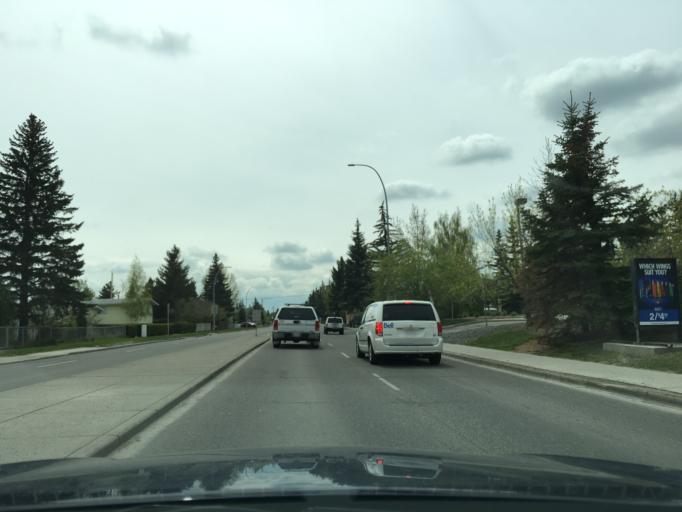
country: CA
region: Alberta
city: Calgary
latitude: 50.9612
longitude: -114.0849
